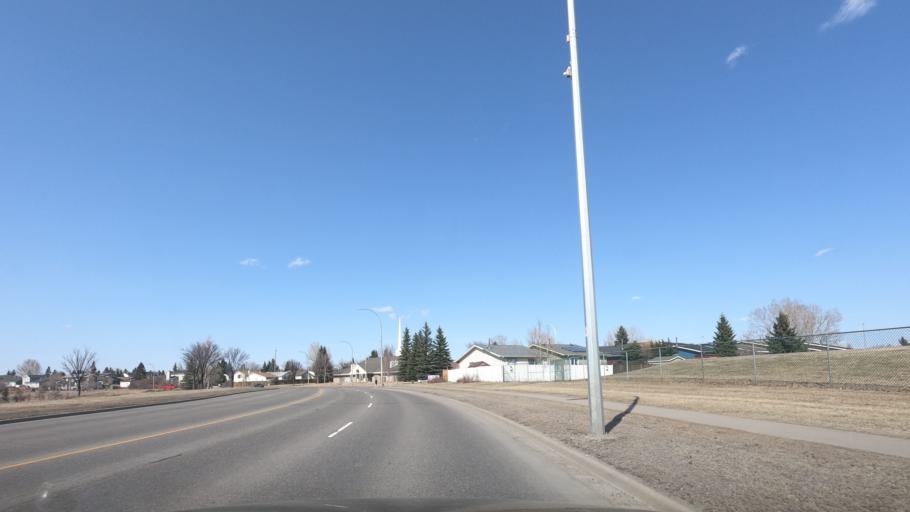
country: CA
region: Alberta
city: Airdrie
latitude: 51.2788
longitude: -114.0088
